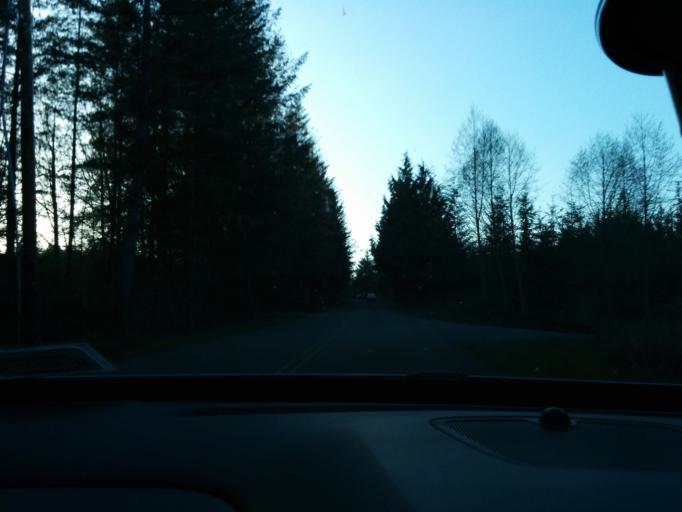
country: US
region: Washington
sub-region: Snohomish County
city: Gold Bar
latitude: 47.8905
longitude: -121.7369
